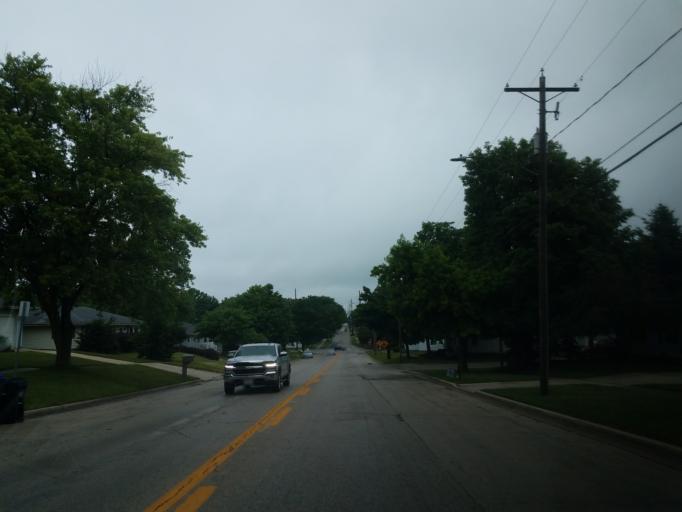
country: US
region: Illinois
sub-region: McLean County
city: Bloomington
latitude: 40.4654
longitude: -88.9817
